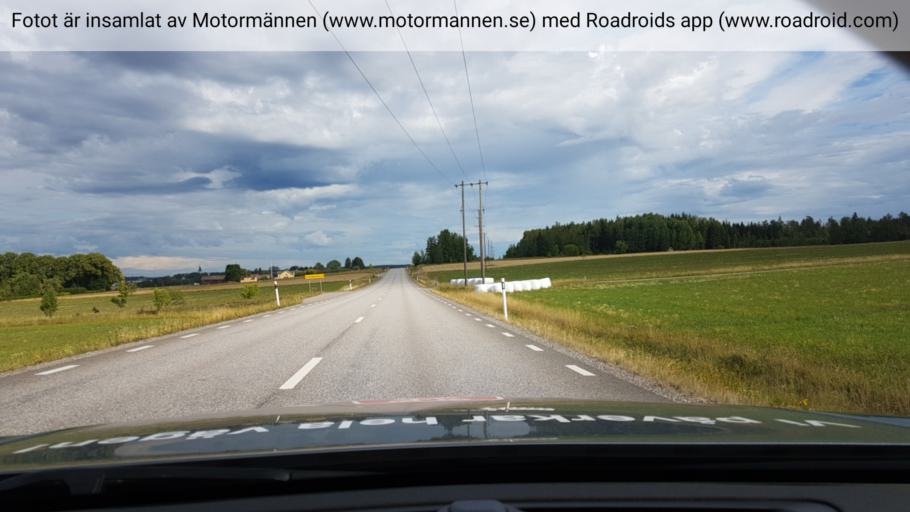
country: SE
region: Uppsala
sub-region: Heby Kommun
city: Heby
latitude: 59.9201
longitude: 16.8823
